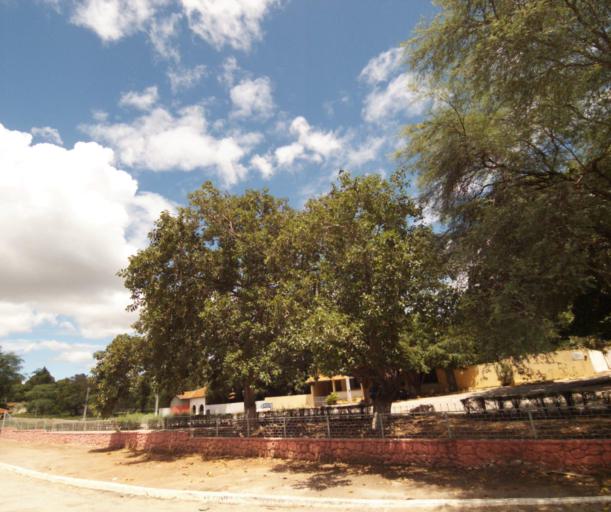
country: BR
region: Bahia
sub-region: Brumado
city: Brumado
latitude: -14.2407
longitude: -41.7241
